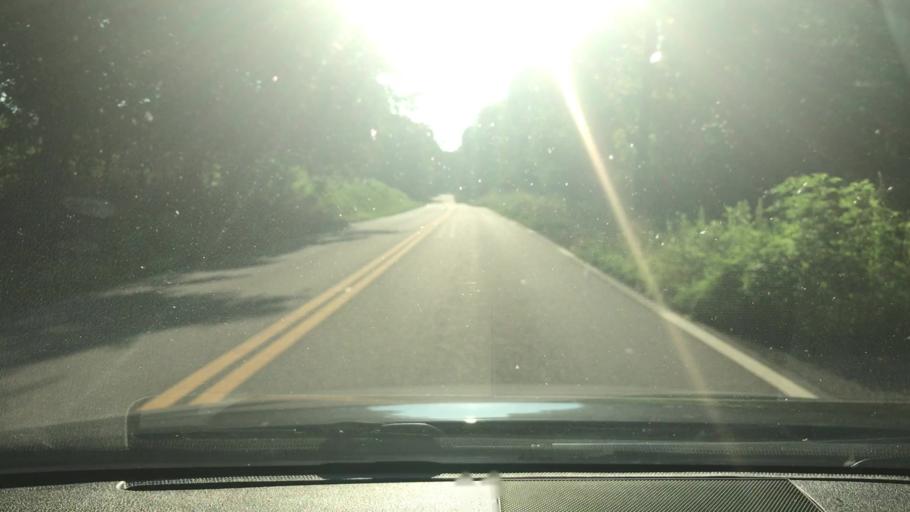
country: US
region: Tennessee
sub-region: Cheatham County
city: Ashland City
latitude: 36.2879
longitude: -87.1610
